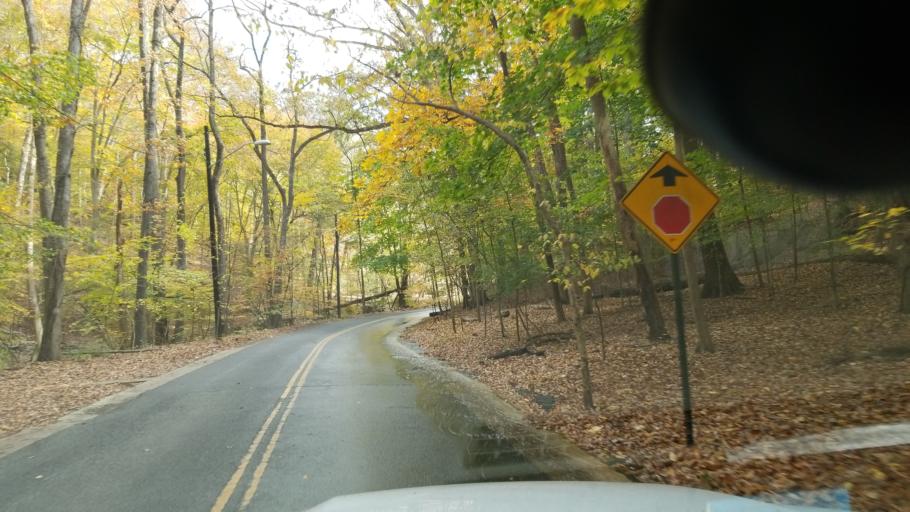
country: US
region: Maryland
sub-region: Montgomery County
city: Chevy Chase
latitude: 38.9576
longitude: -77.0594
